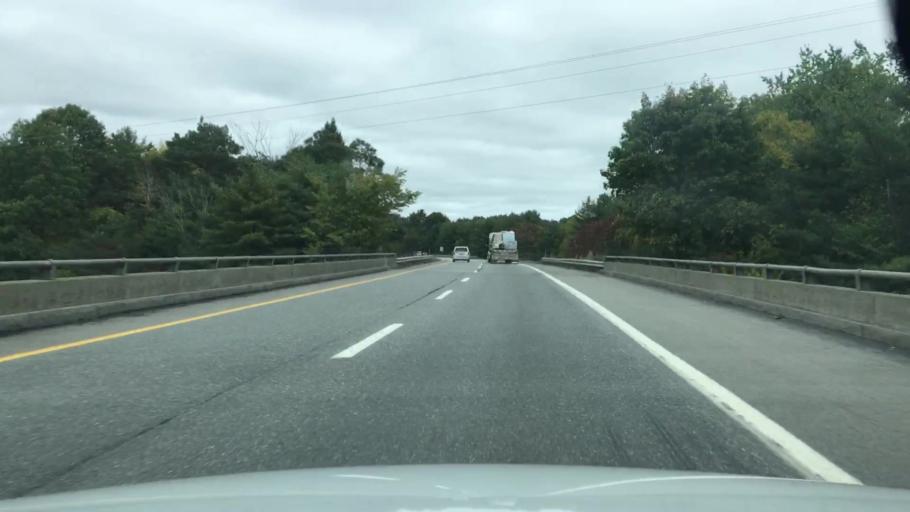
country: US
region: Maine
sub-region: Somerset County
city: Fairfield
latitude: 44.6022
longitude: -69.5831
